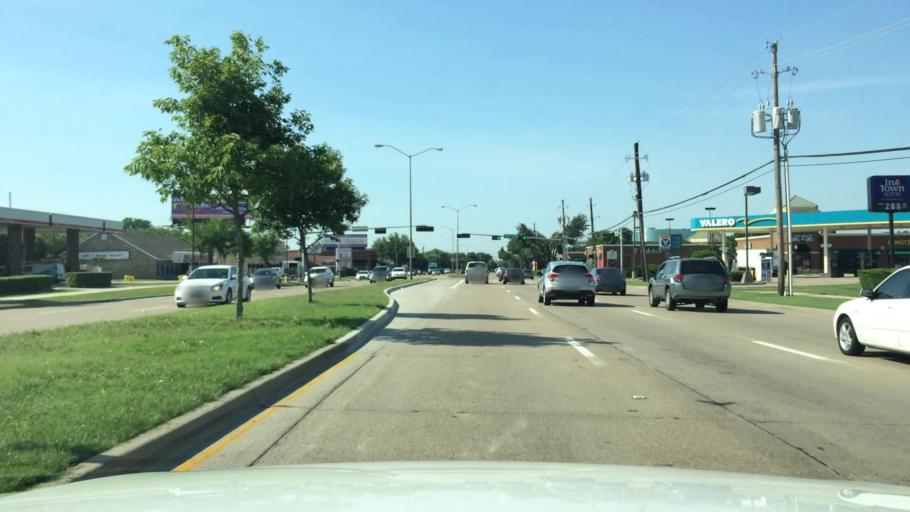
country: US
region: Texas
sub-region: Dallas County
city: Addison
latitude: 33.0085
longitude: -96.7955
